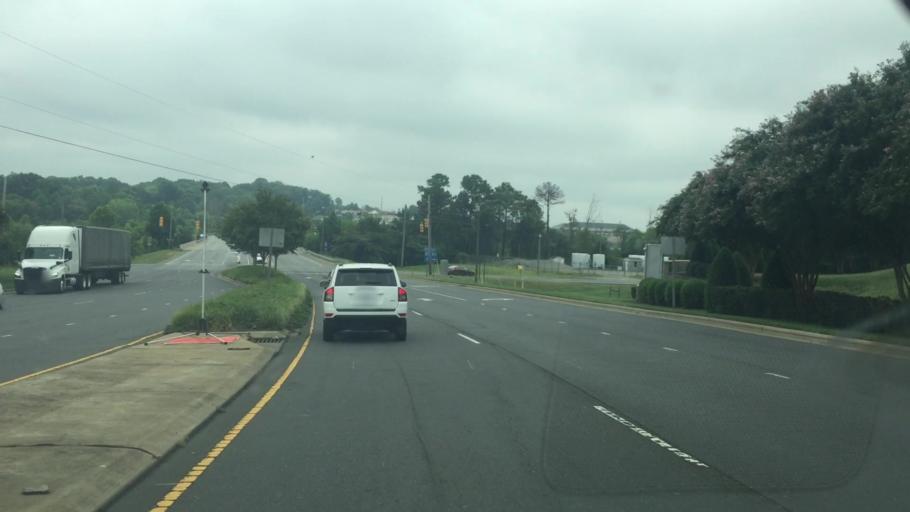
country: US
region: North Carolina
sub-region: Cabarrus County
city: Kannapolis
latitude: 35.4203
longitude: -80.6748
